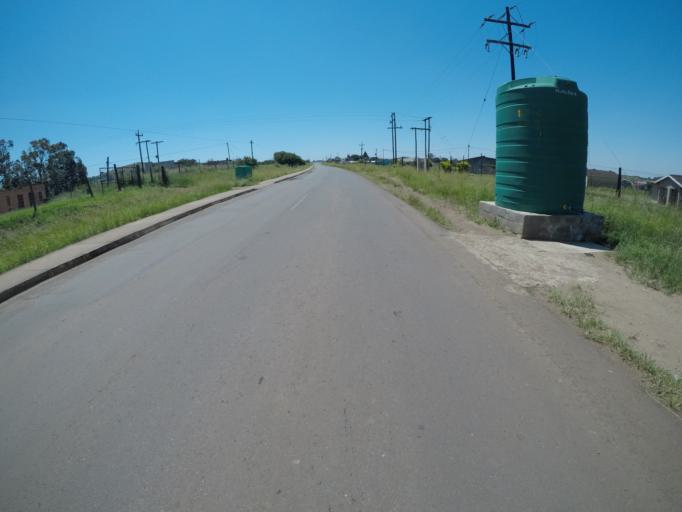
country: ZA
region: KwaZulu-Natal
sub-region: uThungulu District Municipality
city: Empangeni
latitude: -28.7138
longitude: 31.8661
